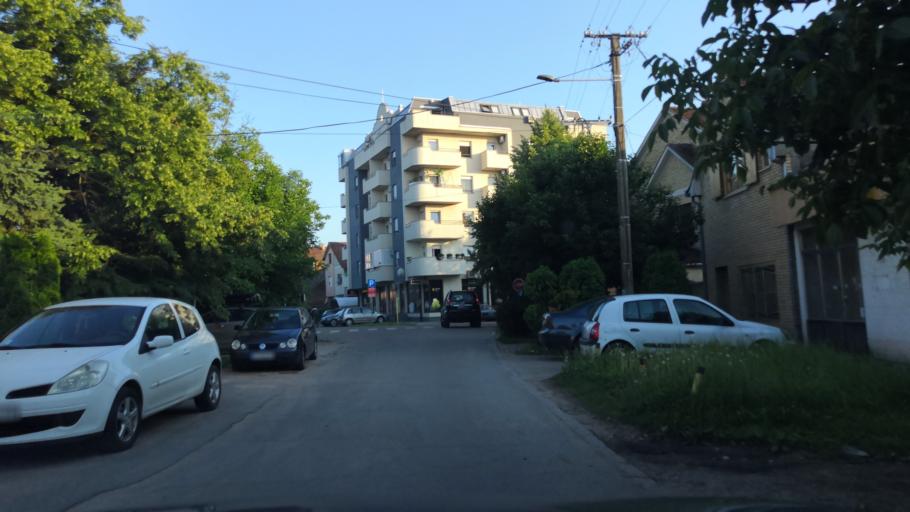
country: RS
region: Autonomna Pokrajina Vojvodina
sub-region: Sremski Okrug
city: Stara Pazova
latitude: 44.9877
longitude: 20.1618
